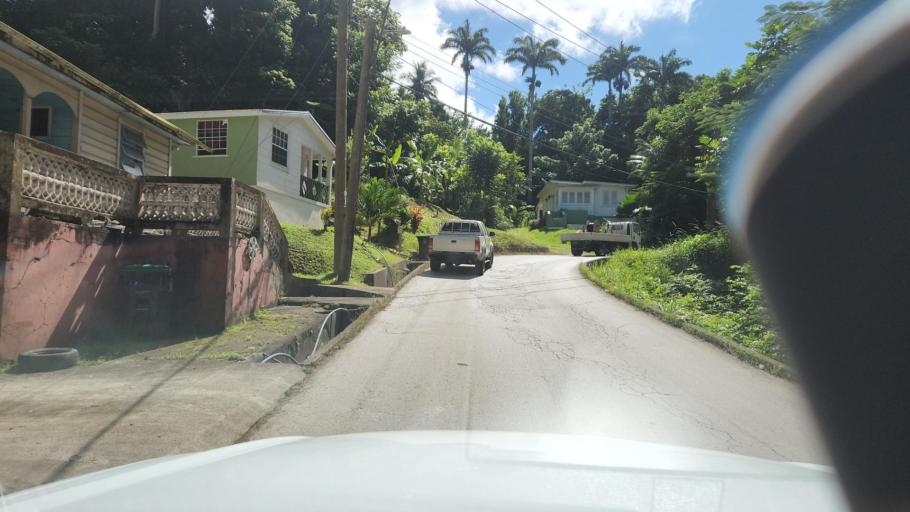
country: BB
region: Saint Thomas
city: Welchman Hall
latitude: 13.2023
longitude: -59.5596
